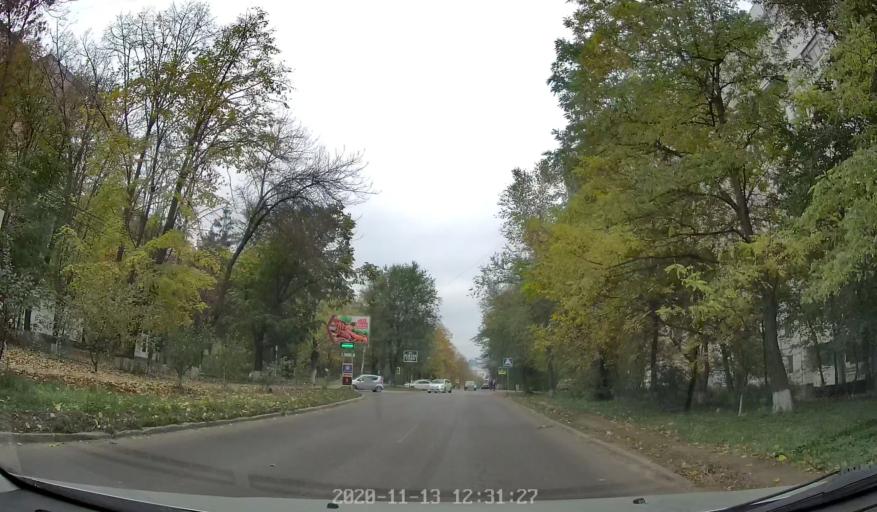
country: MD
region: Chisinau
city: Chisinau
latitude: 46.9791
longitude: 28.8370
